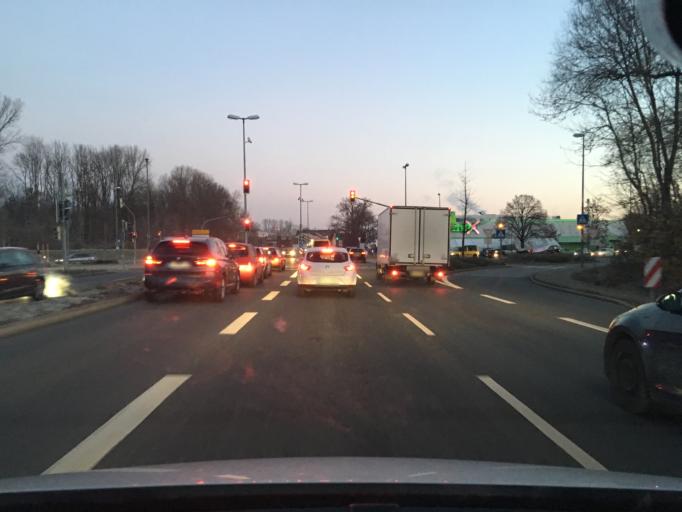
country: DE
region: Bavaria
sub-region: Upper Bavaria
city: Rosenheim
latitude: 47.8391
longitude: 12.1217
